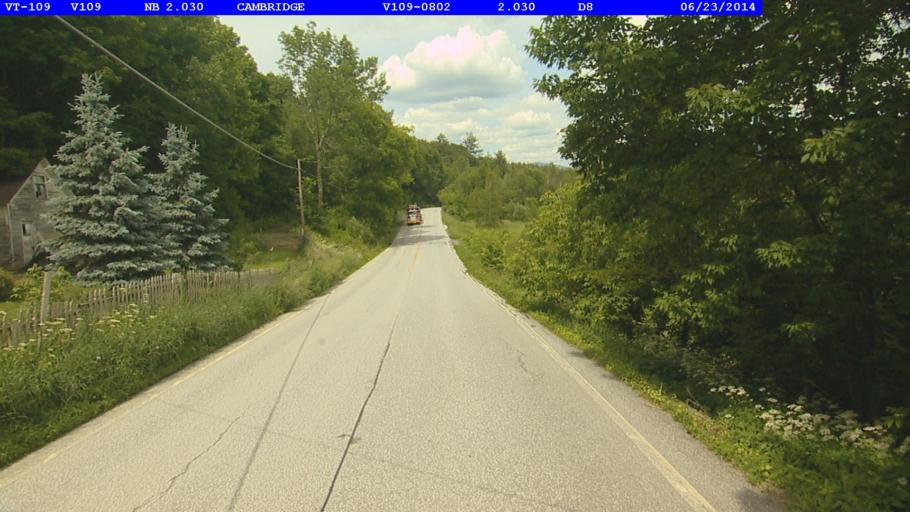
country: US
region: Vermont
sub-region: Lamoille County
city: Johnson
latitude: 44.6677
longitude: -72.7985
